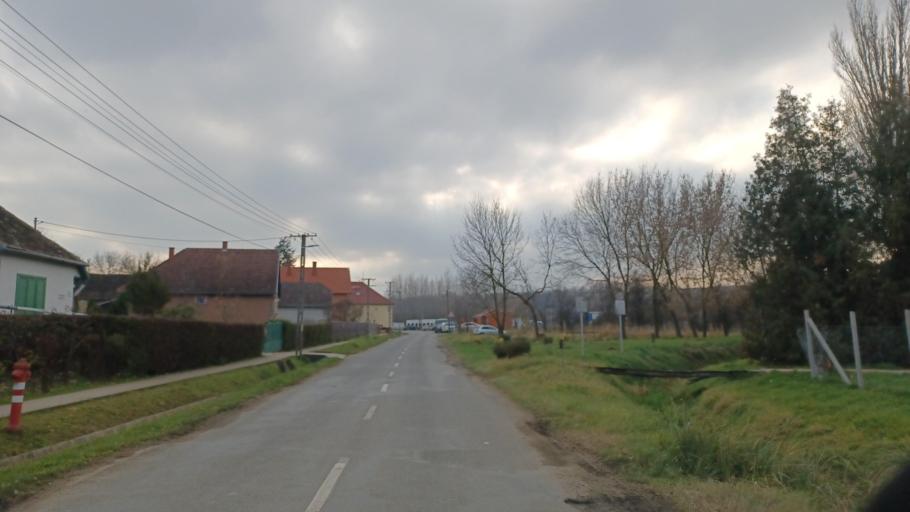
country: HU
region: Tolna
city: Gyonk
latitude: 46.5353
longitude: 18.4452
